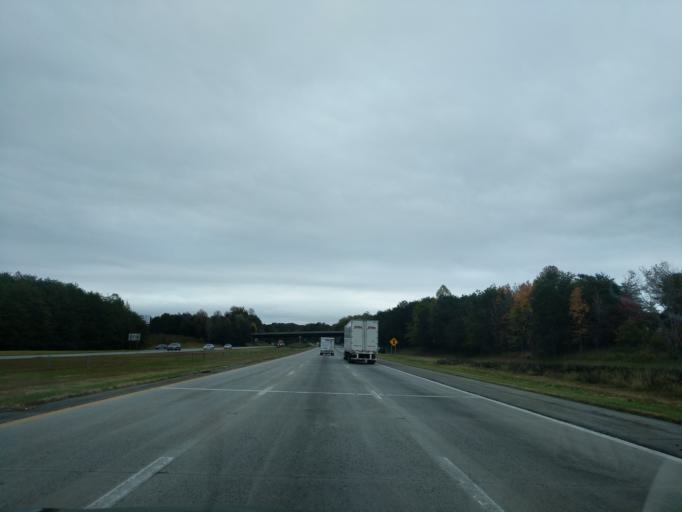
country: US
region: North Carolina
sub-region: Davidson County
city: Thomasville
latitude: 35.8543
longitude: -80.1007
